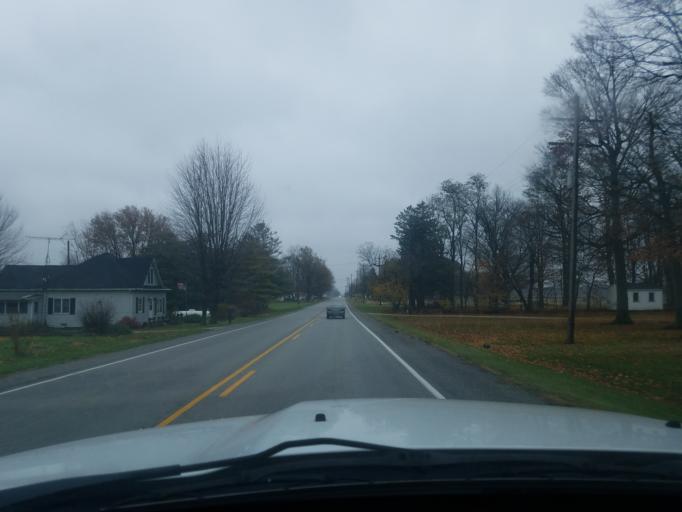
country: US
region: Indiana
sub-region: Howard County
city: Greentown
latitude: 40.4211
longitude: -85.9230
